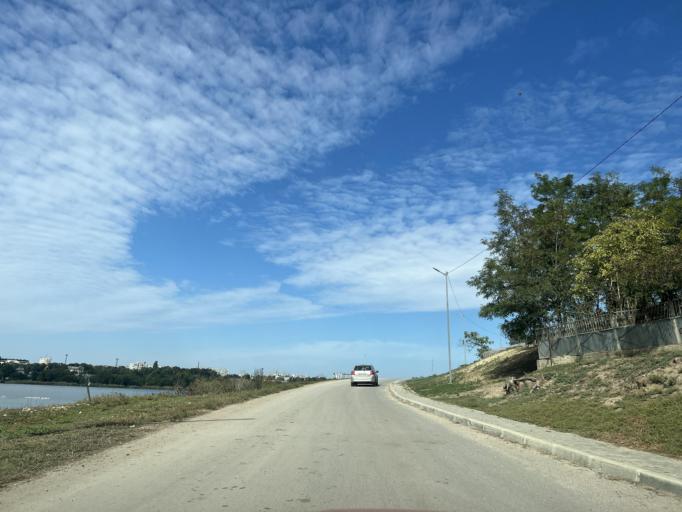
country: MD
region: Ungheni
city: Ungheni
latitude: 47.1993
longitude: 27.8098
